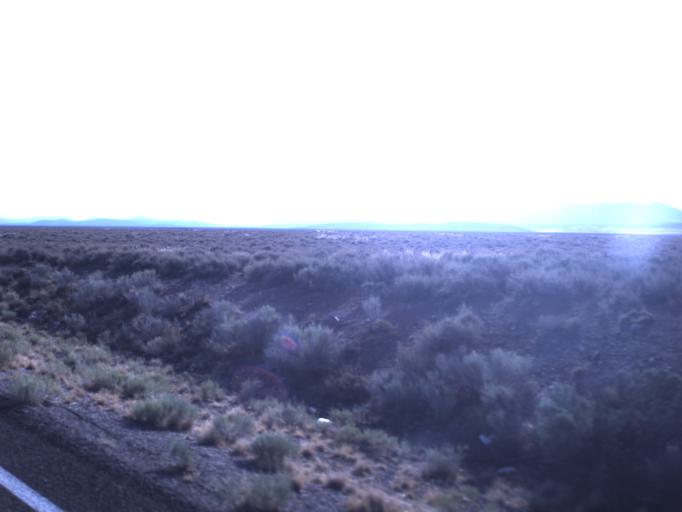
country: US
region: Utah
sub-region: Iron County
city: Enoch
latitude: 37.9393
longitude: -113.0230
